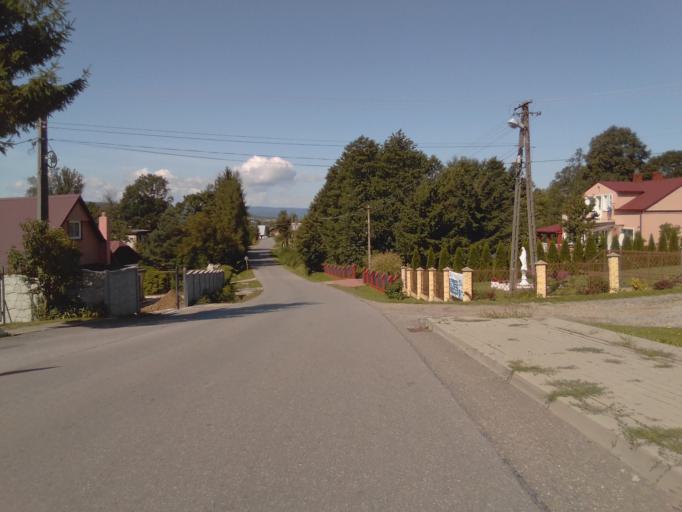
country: PL
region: Subcarpathian Voivodeship
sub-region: Powiat krosnienski
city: Chorkowka
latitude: 49.6052
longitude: 21.6662
